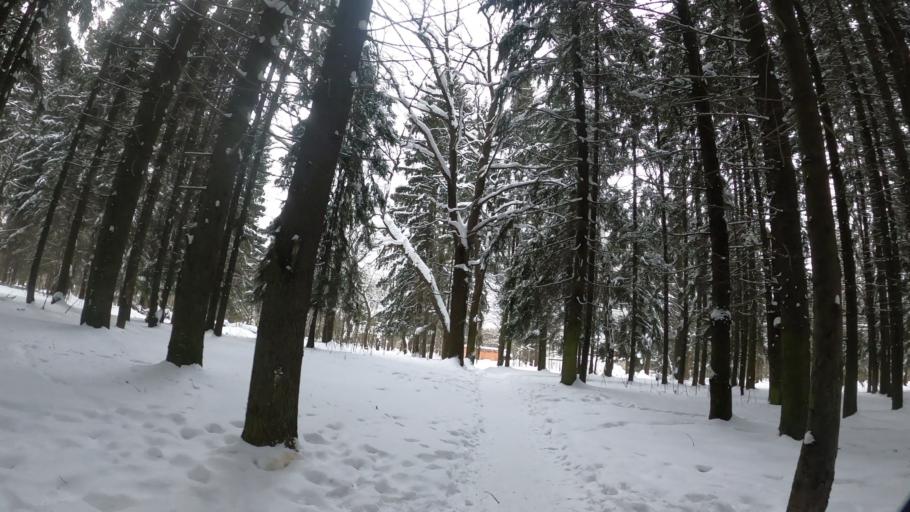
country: RU
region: Moskovskaya
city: Lugovaya
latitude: 56.0493
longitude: 37.4955
